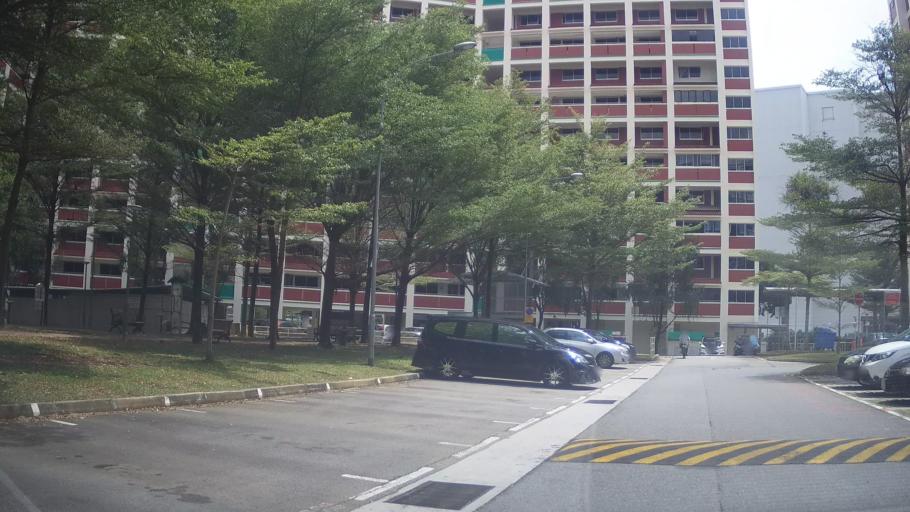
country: SG
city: Singapore
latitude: 1.3275
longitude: 103.7214
